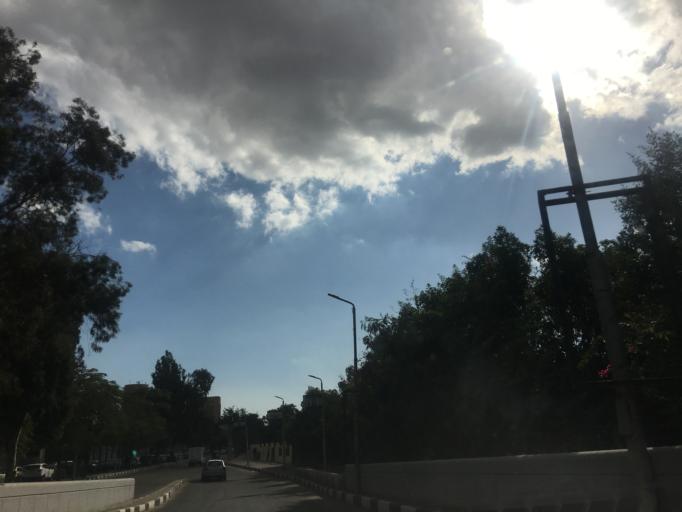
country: EG
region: Muhafazat al Qahirah
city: Cairo
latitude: 30.0469
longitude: 31.2197
